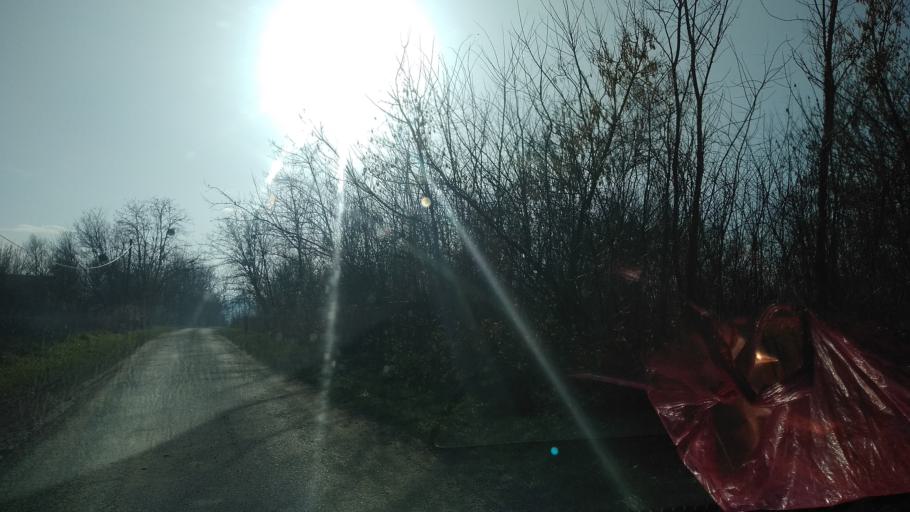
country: HU
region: Somogy
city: Barcs
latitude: 45.9557
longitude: 17.4868
